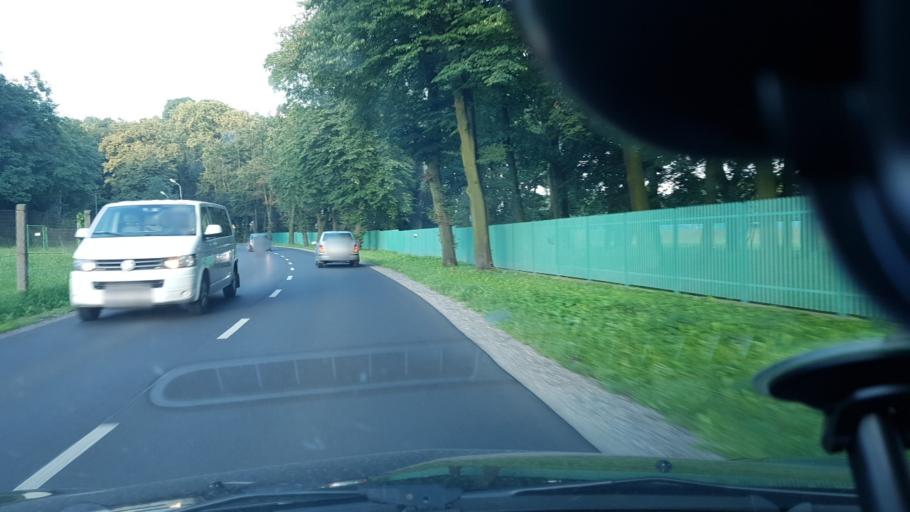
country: PL
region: Lesser Poland Voivodeship
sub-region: Powiat krakowski
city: Kryspinow
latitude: 50.0390
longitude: 19.8352
